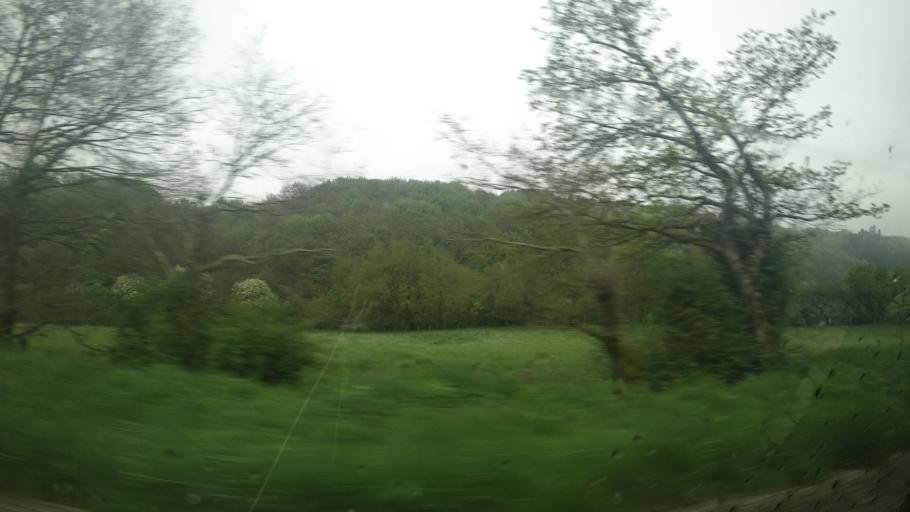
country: FR
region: Midi-Pyrenees
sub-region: Departement de l'Aveyron
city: Salles-Curan
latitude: 44.2653
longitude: 2.8886
